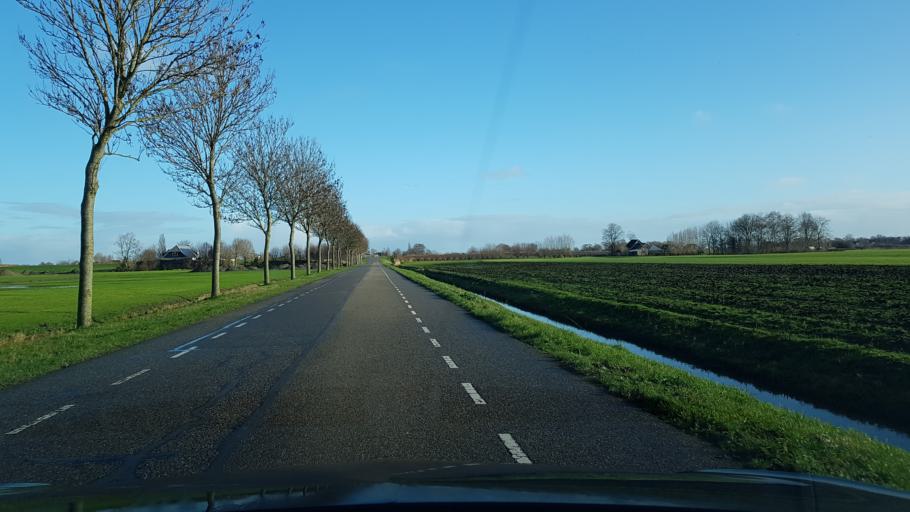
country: NL
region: North Holland
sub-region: Gemeente Uithoorn
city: Uithoorn
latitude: 52.1877
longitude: 4.8143
